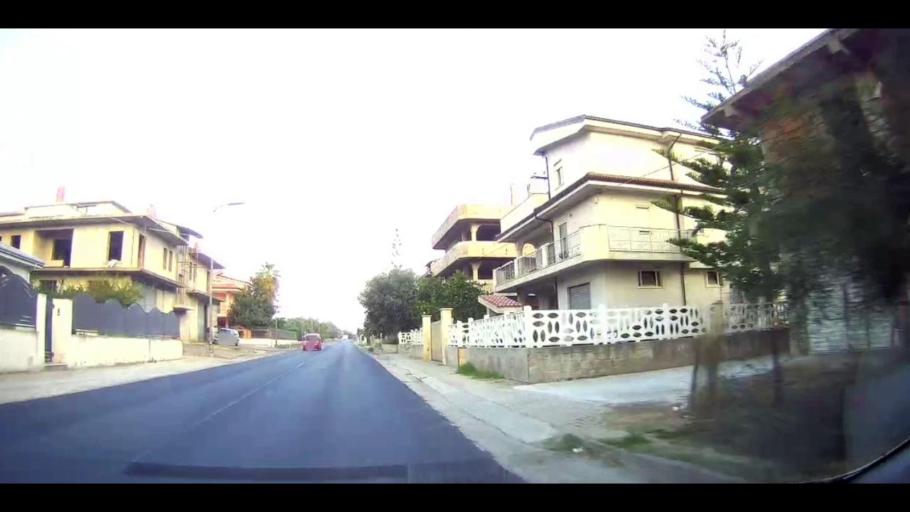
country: IT
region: Calabria
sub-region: Provincia di Crotone
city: Torretta
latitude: 39.4578
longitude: 17.0318
